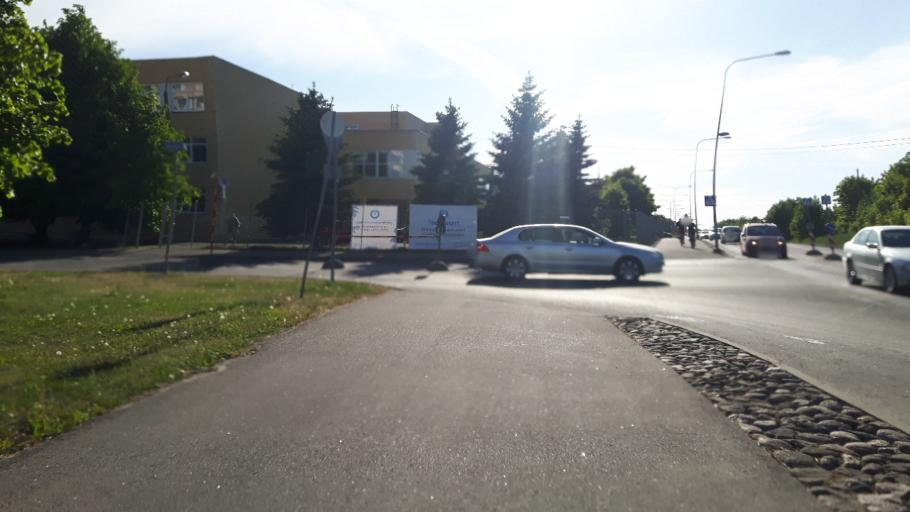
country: EE
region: Harju
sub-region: Tallinna linn
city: Kose
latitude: 59.4512
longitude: 24.8466
